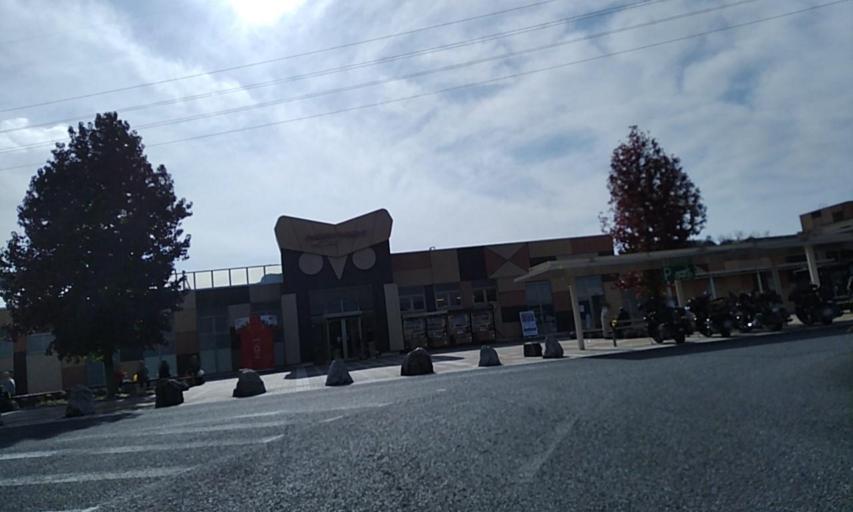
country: JP
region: Aichi
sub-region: Toyota-shi
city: Toyota
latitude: 35.0347
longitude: 137.2224
